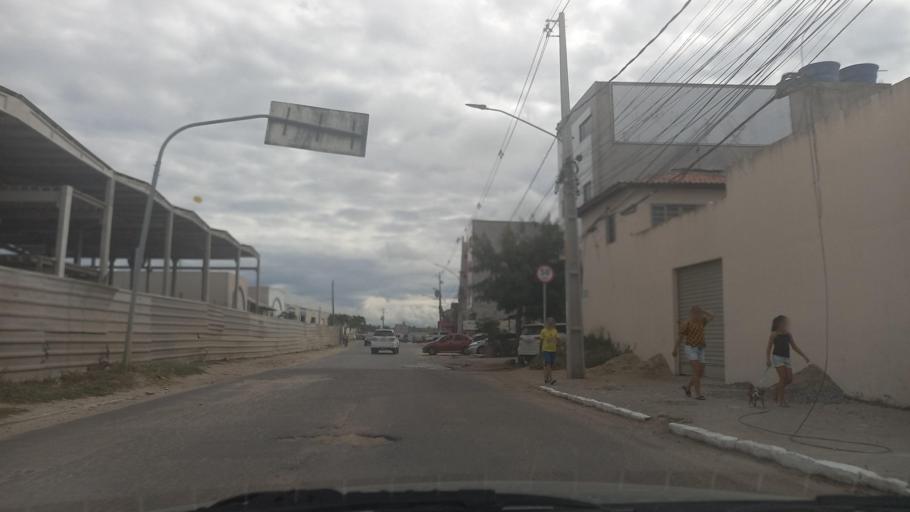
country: BR
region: Pernambuco
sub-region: Caruaru
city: Caruaru
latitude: -8.2872
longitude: -36.0042
